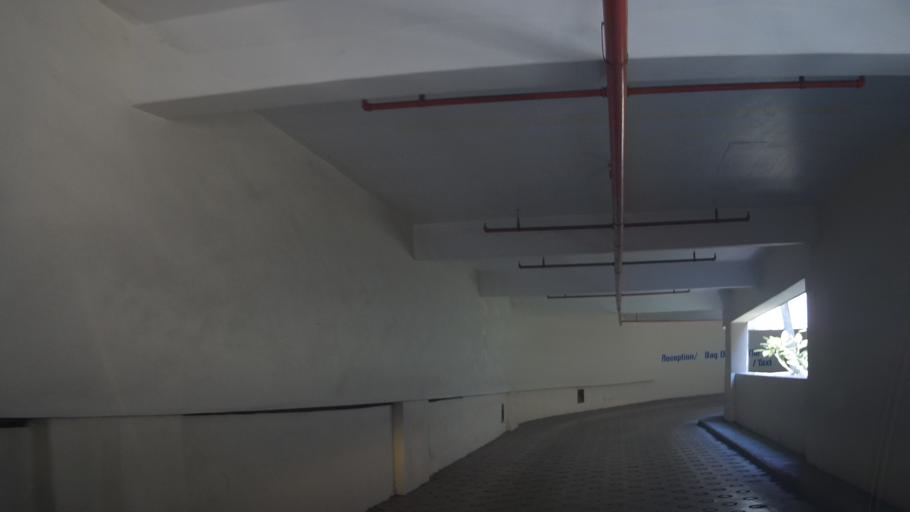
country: SG
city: Singapore
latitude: 1.3228
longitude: 103.9620
